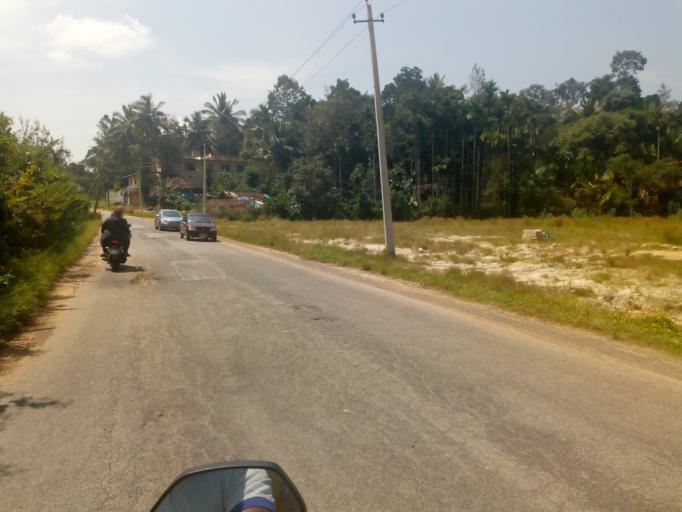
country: IN
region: Karnataka
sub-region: Kodagu
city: Ponnampet
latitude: 12.1245
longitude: 75.9412
